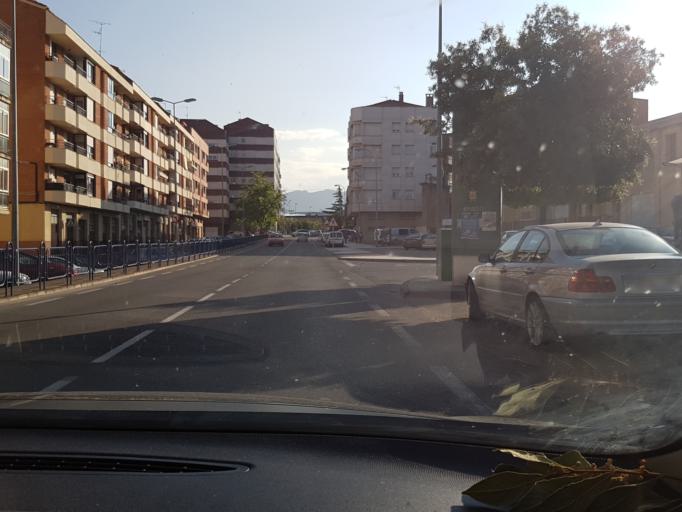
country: ES
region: La Rioja
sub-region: Provincia de La Rioja
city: Arnedo
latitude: 42.2240
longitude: -2.1021
